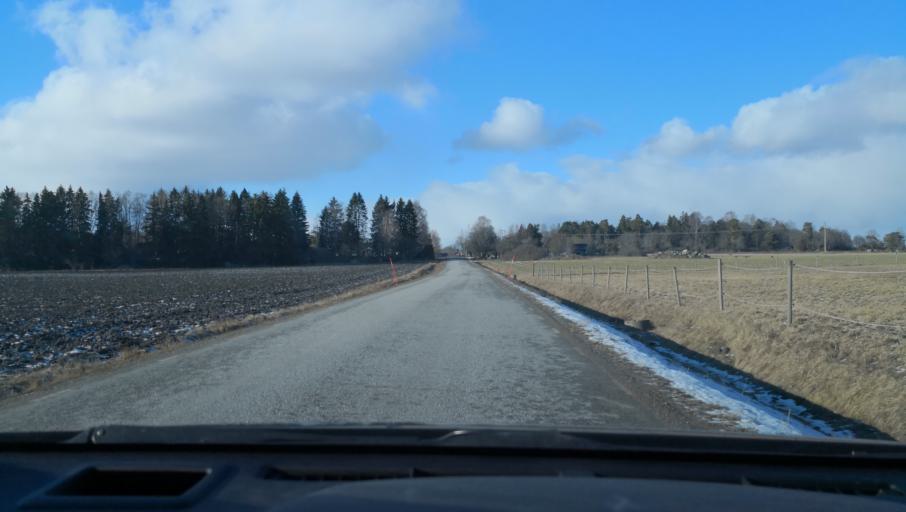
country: SE
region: Uppsala
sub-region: Enkopings Kommun
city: Hummelsta
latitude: 59.6336
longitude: 16.9743
